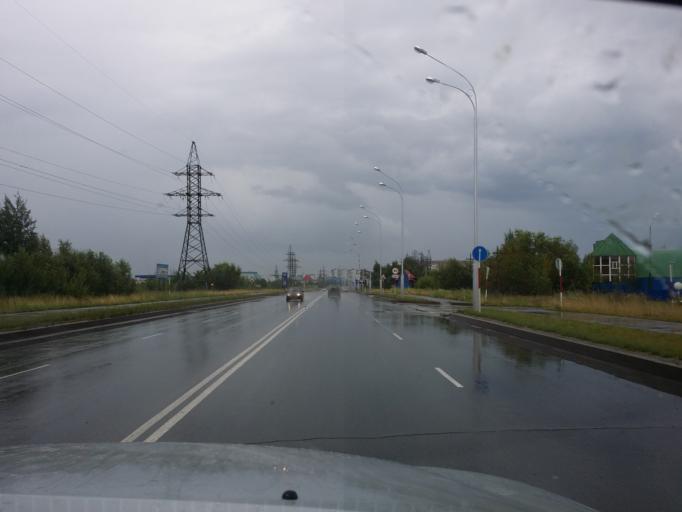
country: RU
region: Khanty-Mansiyskiy Avtonomnyy Okrug
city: Nizhnevartovsk
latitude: 60.9630
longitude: 76.5531
